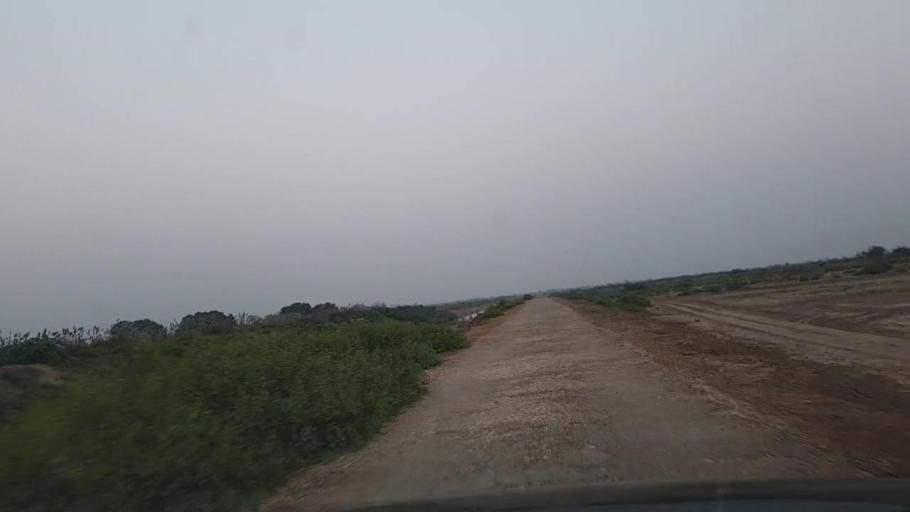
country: PK
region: Sindh
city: Mirpur Sakro
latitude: 24.6350
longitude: 67.7048
